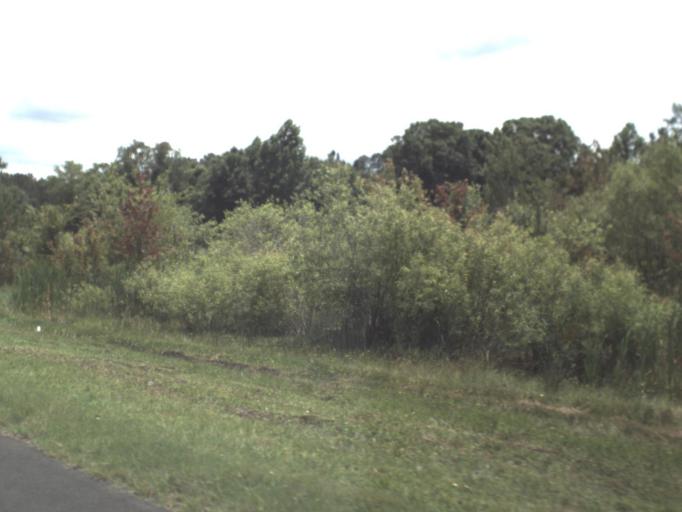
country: US
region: Georgia
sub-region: Camden County
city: Kingsland
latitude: 30.7154
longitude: -81.6747
